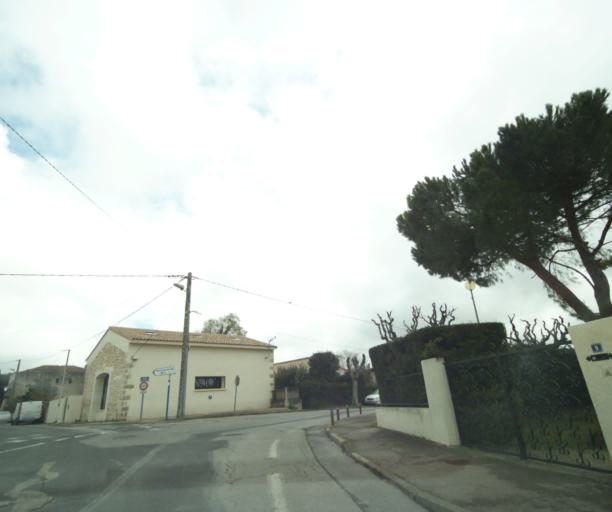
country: FR
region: Languedoc-Roussillon
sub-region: Departement de l'Herault
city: Fabregues
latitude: 43.5518
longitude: 3.7736
